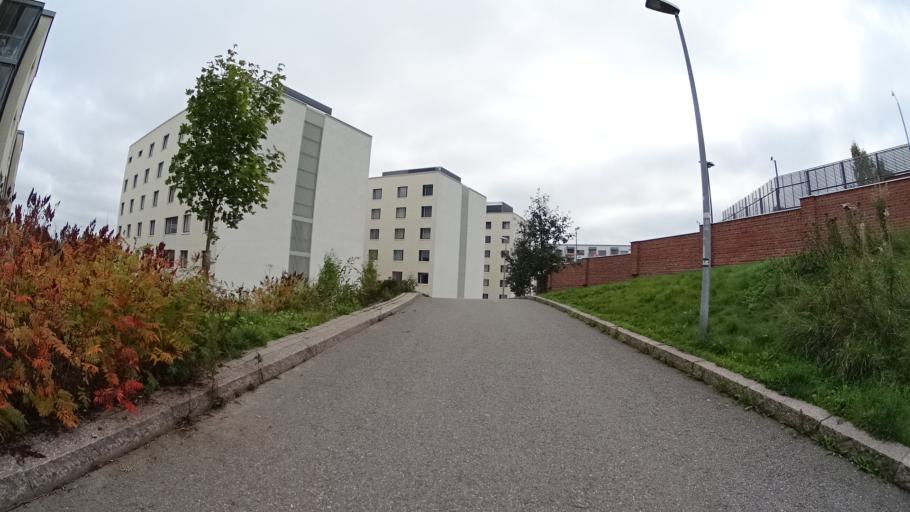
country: FI
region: Uusimaa
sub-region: Helsinki
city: Helsinki
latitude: 60.1965
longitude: 24.9703
